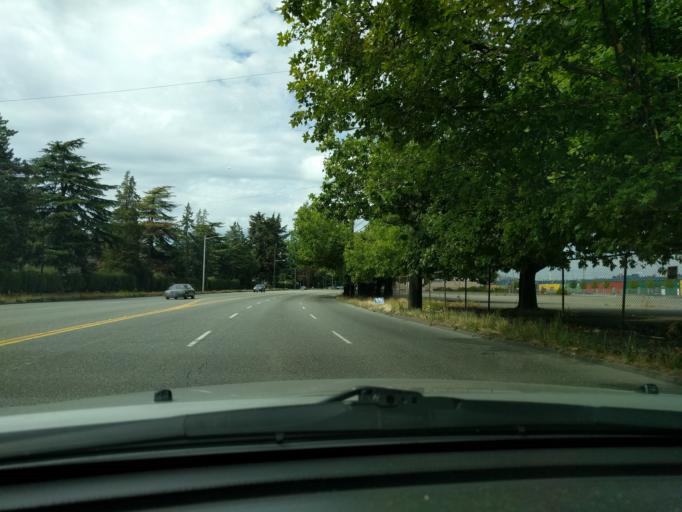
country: US
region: Washington
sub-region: King County
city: White Center
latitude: 47.5578
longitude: -122.3392
